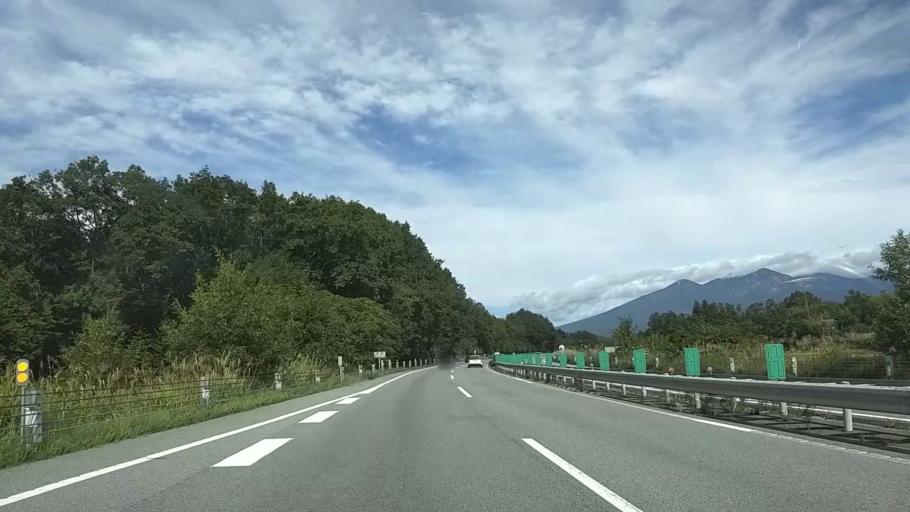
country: JP
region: Yamanashi
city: Nirasaki
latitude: 35.7946
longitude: 138.3975
